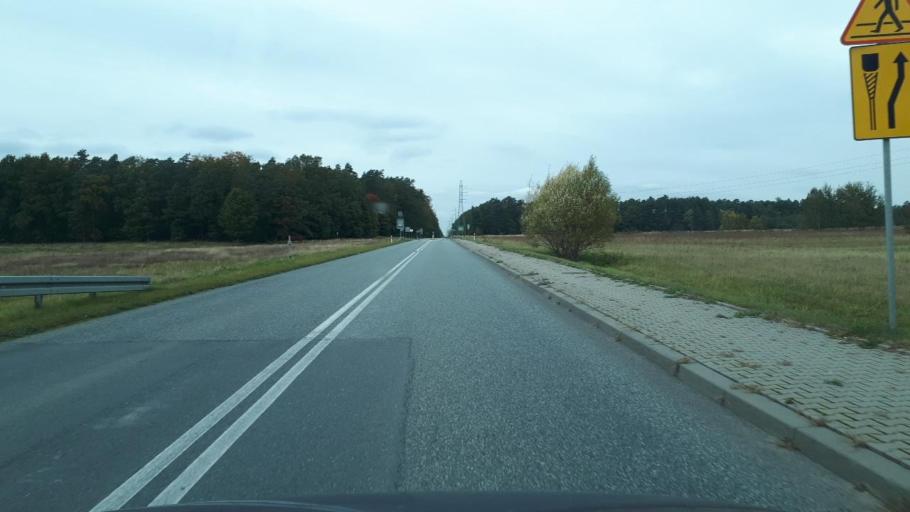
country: PL
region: Opole Voivodeship
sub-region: Powiat oleski
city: Dobrodzien
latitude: 50.7798
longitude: 18.4245
